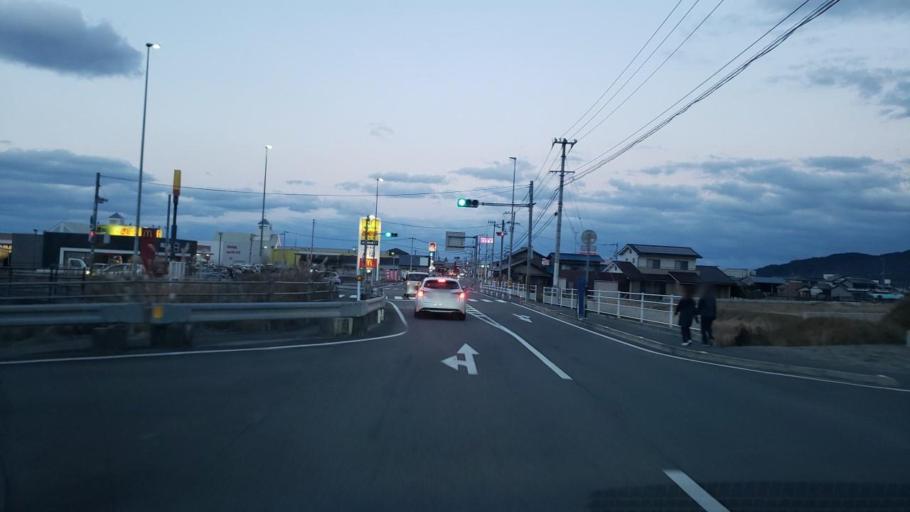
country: JP
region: Tokushima
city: Kamojimacho-jogejima
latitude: 34.2395
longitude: 134.3530
